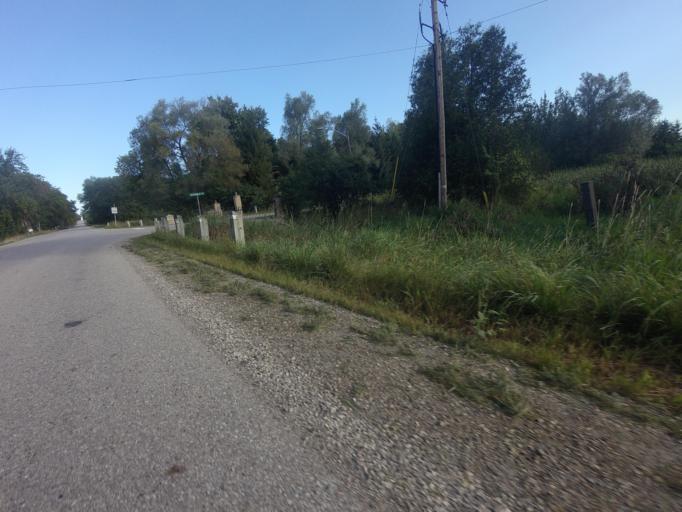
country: CA
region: Ontario
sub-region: Wellington County
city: Guelph
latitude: 43.6085
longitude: -80.3576
